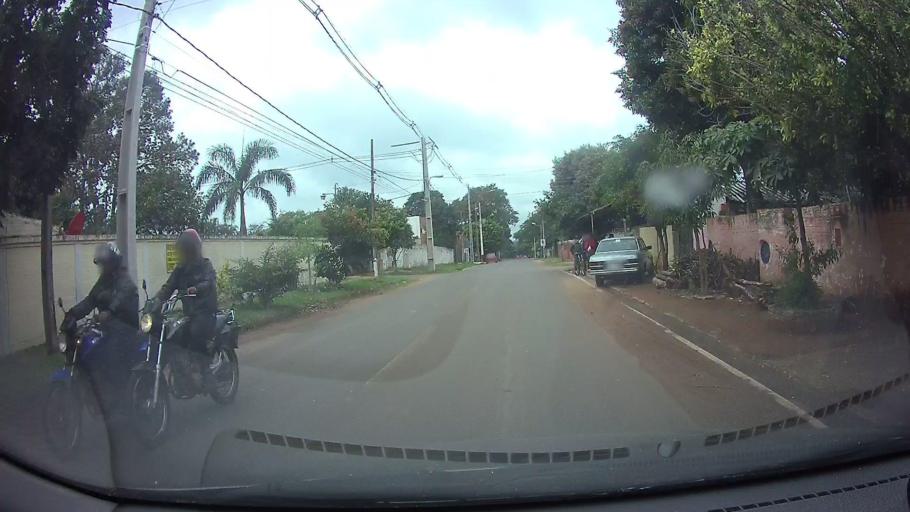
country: PY
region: Central
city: San Lorenzo
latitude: -25.3209
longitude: -57.5062
